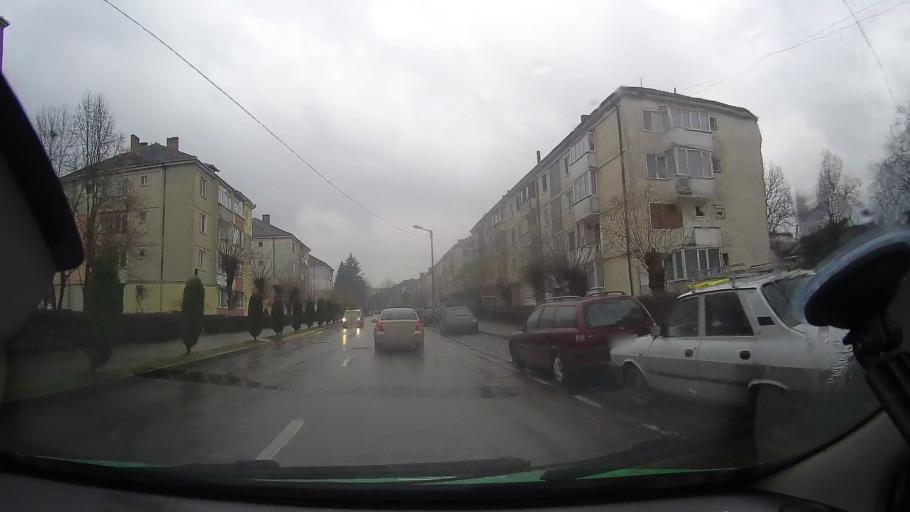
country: RO
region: Hunedoara
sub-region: Municipiul Brad
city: Brad
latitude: 46.1242
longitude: 22.7913
